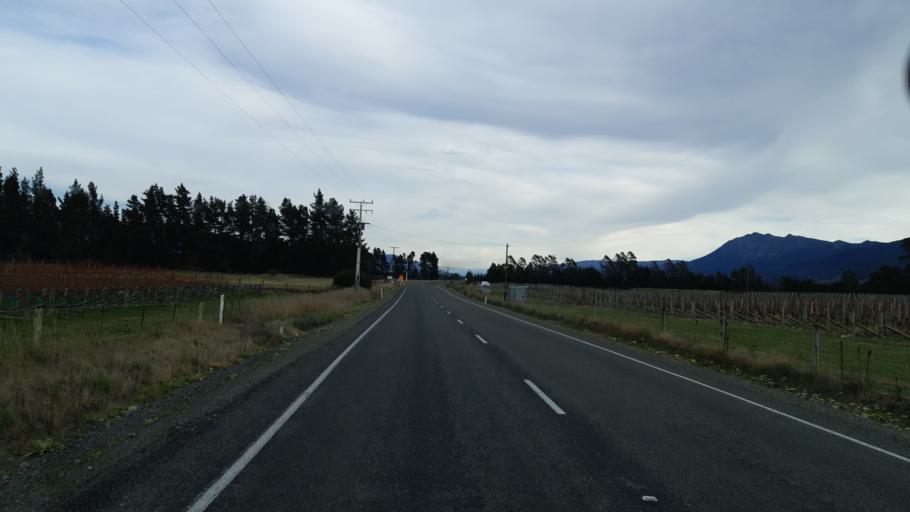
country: NZ
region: Nelson
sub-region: Nelson City
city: Nelson
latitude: -41.6019
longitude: 173.4208
